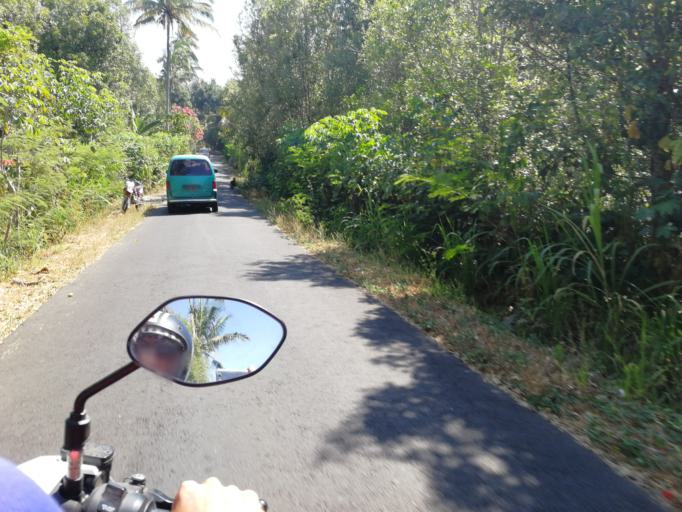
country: ID
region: Bali
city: Banjar Kedisan
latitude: -8.1627
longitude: 115.3048
